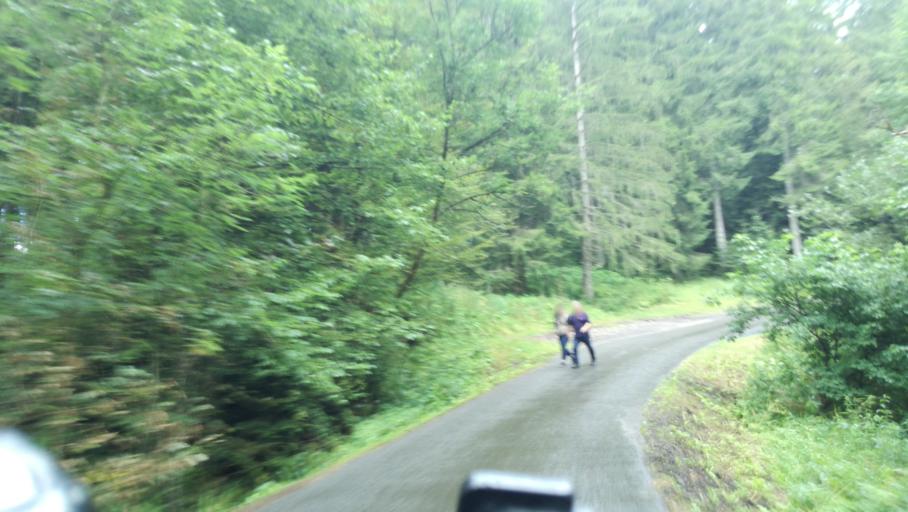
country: CH
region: Zug
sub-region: Zug
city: Walchwil
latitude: 47.1221
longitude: 8.5386
